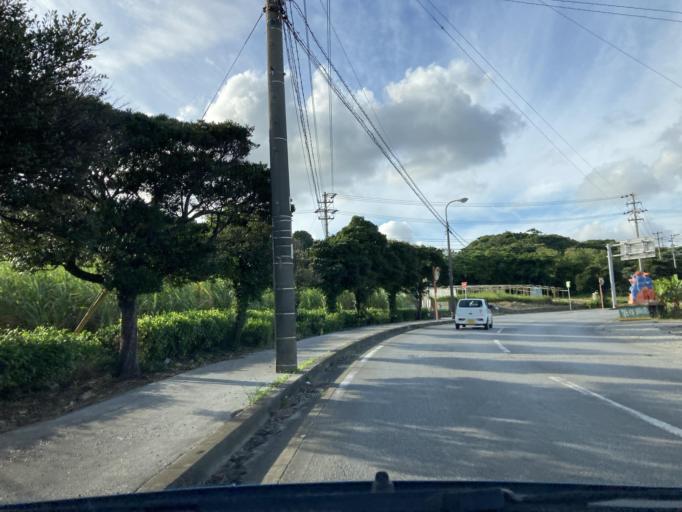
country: JP
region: Okinawa
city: Itoman
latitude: 26.1360
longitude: 127.7467
